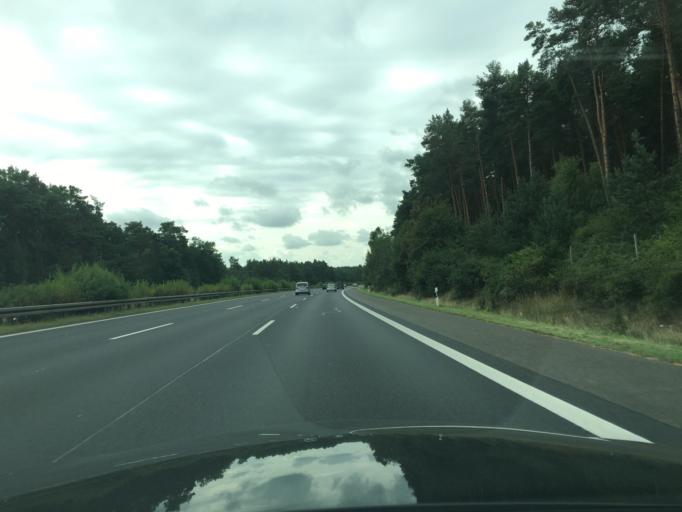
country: DE
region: Brandenburg
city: Beelitz
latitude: 52.2377
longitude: 12.9173
